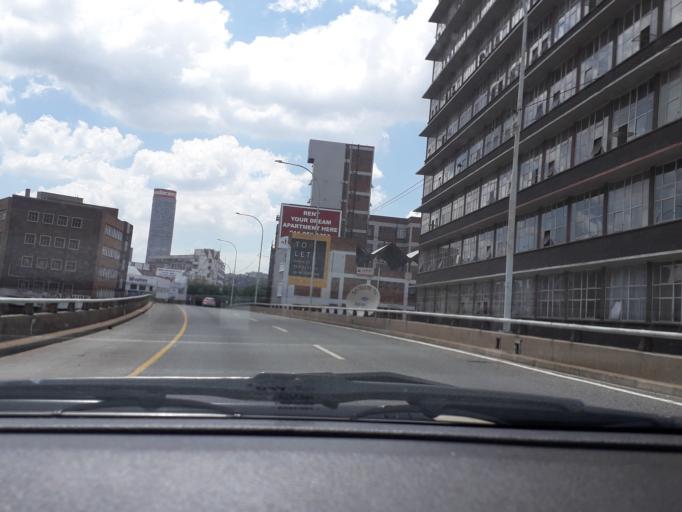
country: ZA
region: Gauteng
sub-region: City of Johannesburg Metropolitan Municipality
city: Johannesburg
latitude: -26.2030
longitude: 28.0549
